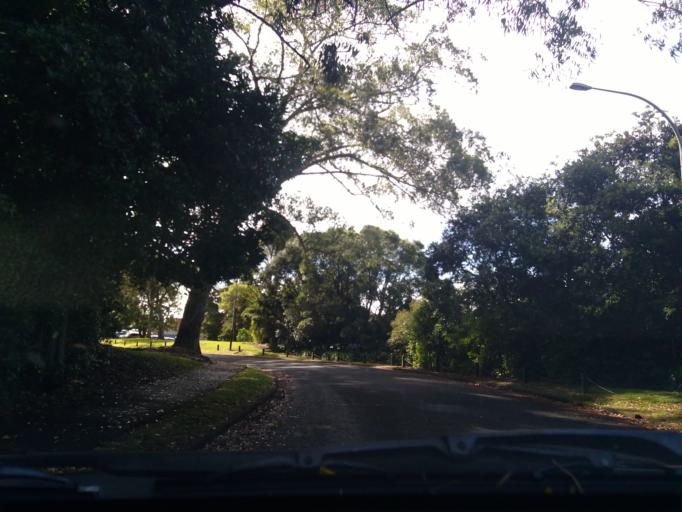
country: NZ
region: Auckland
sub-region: Auckland
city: Auckland
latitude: -36.8733
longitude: 174.7293
